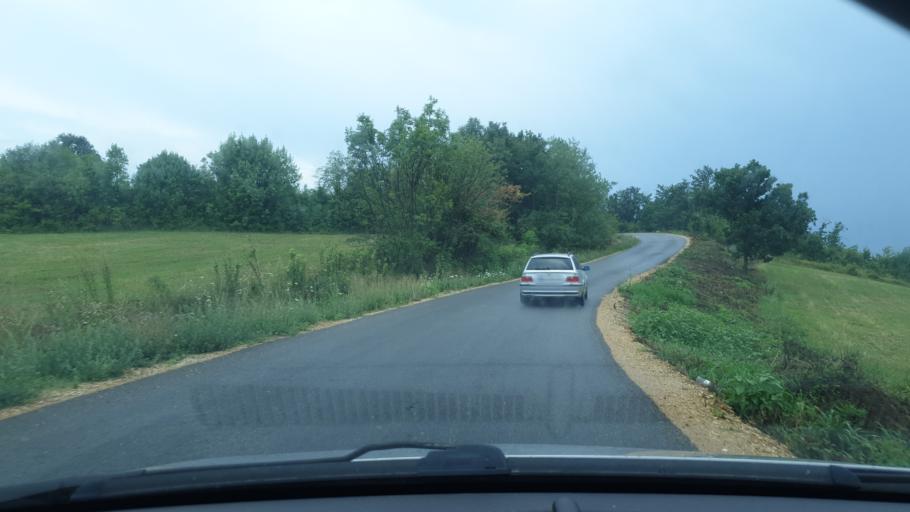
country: RS
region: Central Serbia
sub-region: Sumadijski Okrug
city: Kragujevac
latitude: 44.0570
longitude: 20.7843
